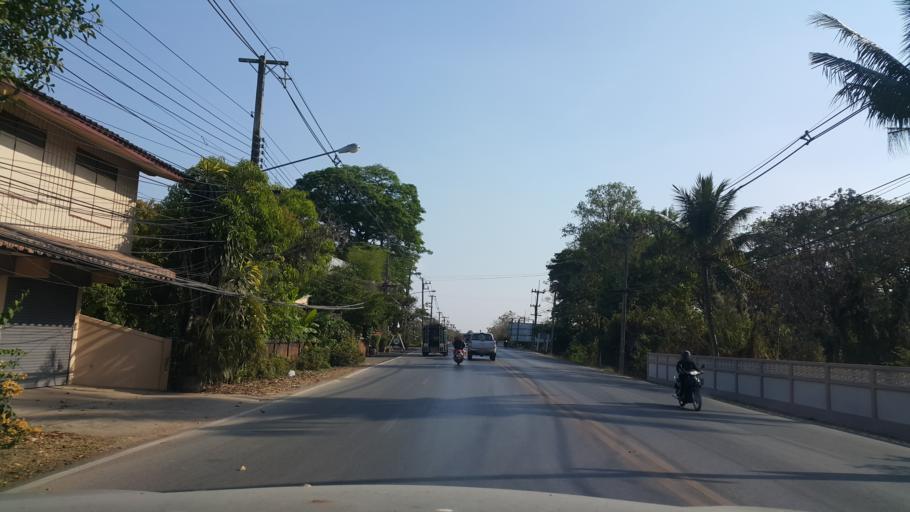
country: TH
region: Chiang Mai
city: San Sai
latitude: 18.8415
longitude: 99.0432
